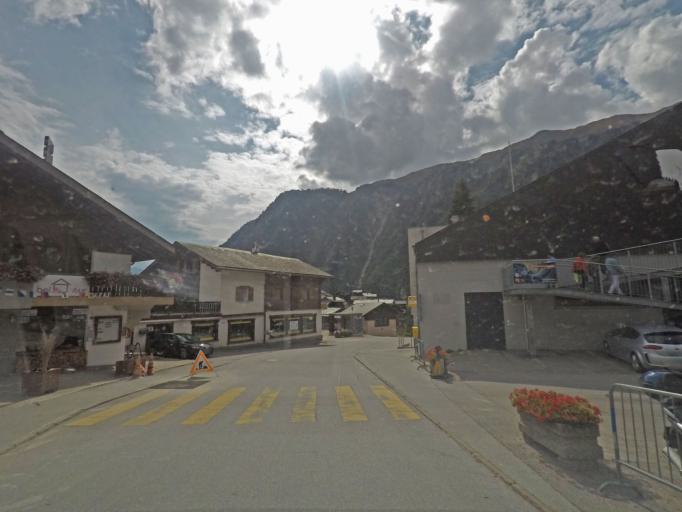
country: CH
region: Valais
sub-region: Brig District
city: Naters
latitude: 46.3590
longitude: 7.9846
